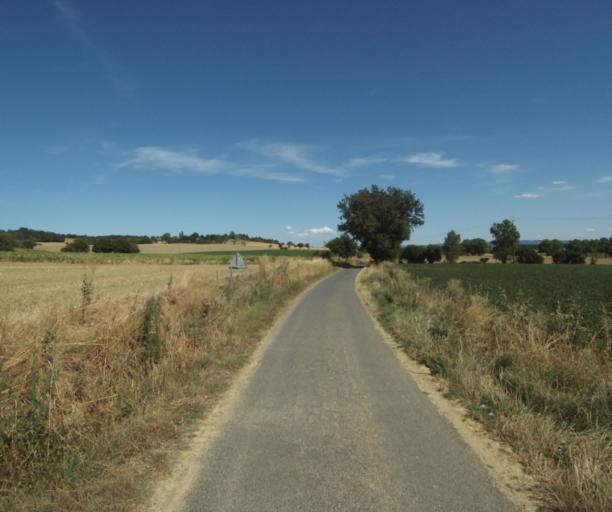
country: FR
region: Midi-Pyrenees
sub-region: Departement de la Haute-Garonne
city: Saint-Felix-Lauragais
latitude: 43.5181
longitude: 1.8981
